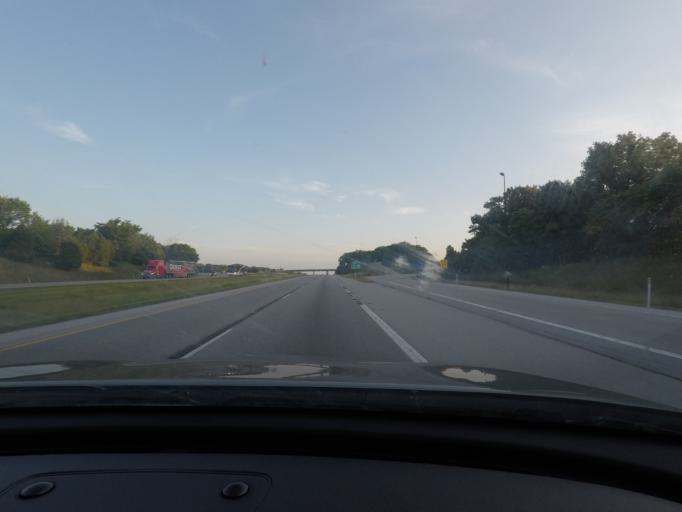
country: US
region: Illinois
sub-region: Johnson County
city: Goreville
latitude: 37.5300
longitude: -88.9209
